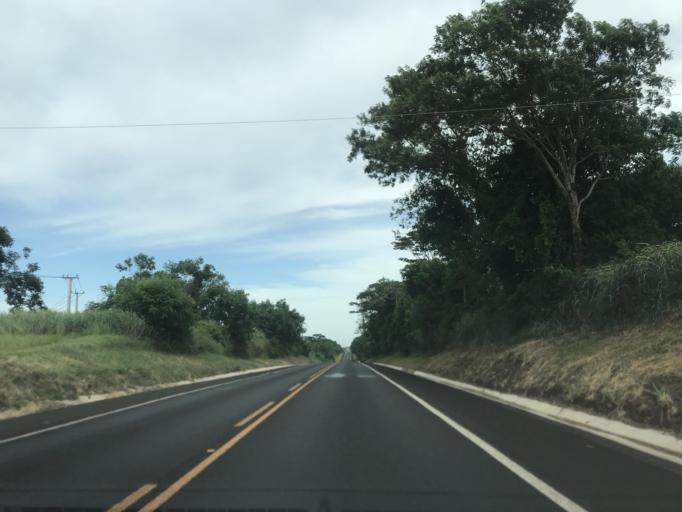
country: BR
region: Parana
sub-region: Paranavai
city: Paranavai
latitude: -23.0233
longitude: -52.4930
